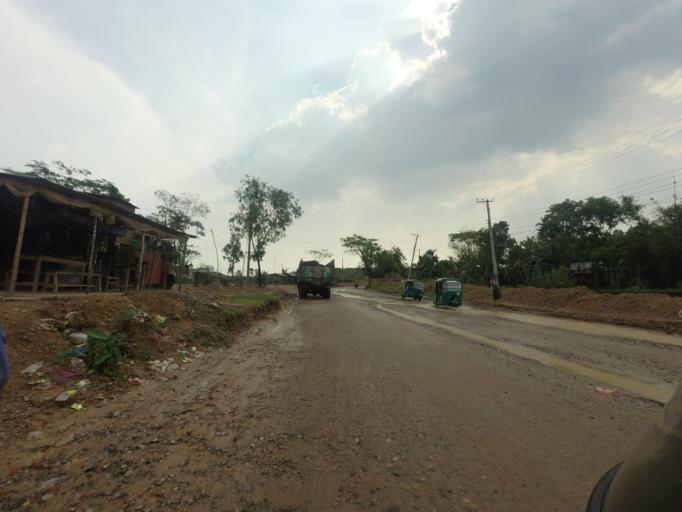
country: BD
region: Sylhet
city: Sylhet
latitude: 24.9517
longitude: 91.8683
